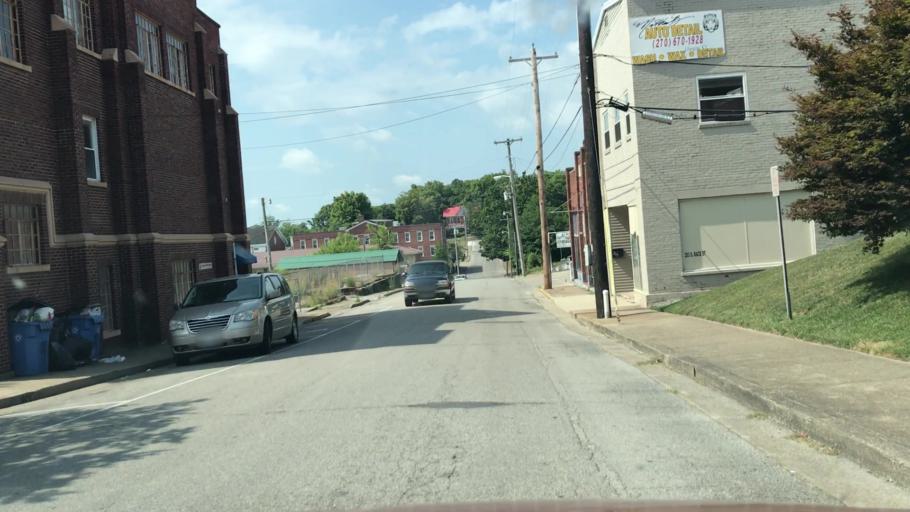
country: US
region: Kentucky
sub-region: Barren County
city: Glasgow
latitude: 36.9953
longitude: -85.9136
